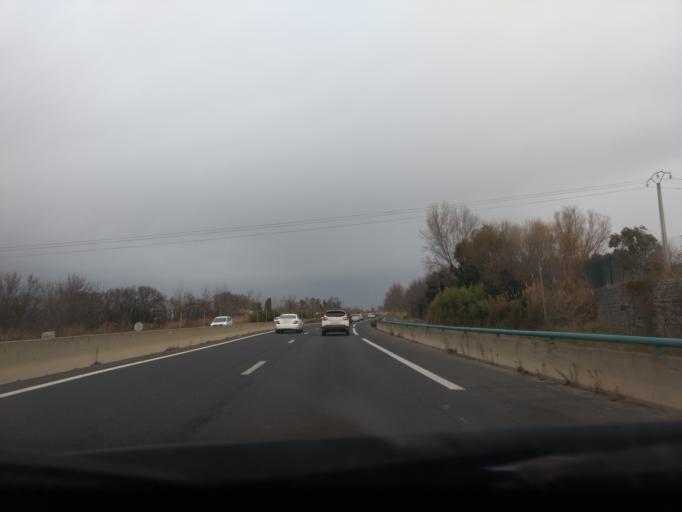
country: FR
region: Languedoc-Roussillon
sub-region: Departement de l'Herault
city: Lattes
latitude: 43.5626
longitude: 3.8942
